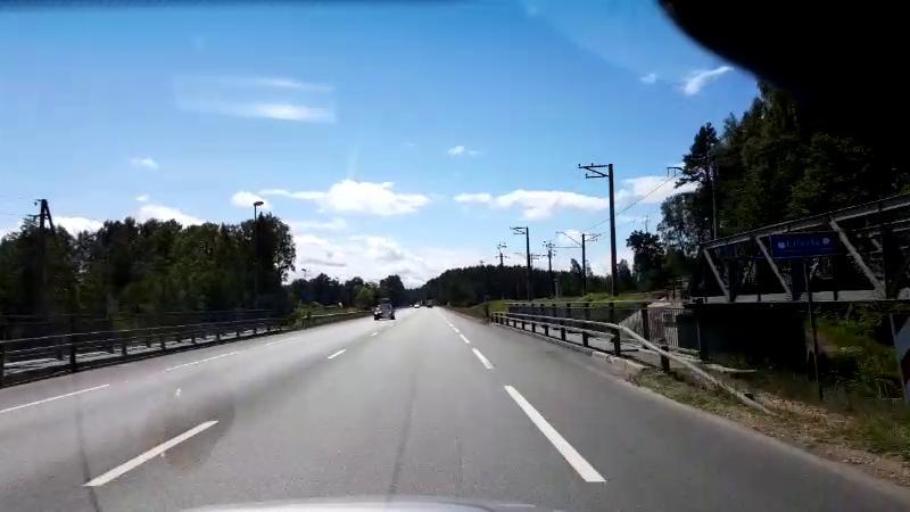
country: LV
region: Carnikava
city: Carnikava
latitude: 57.1852
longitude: 24.3446
